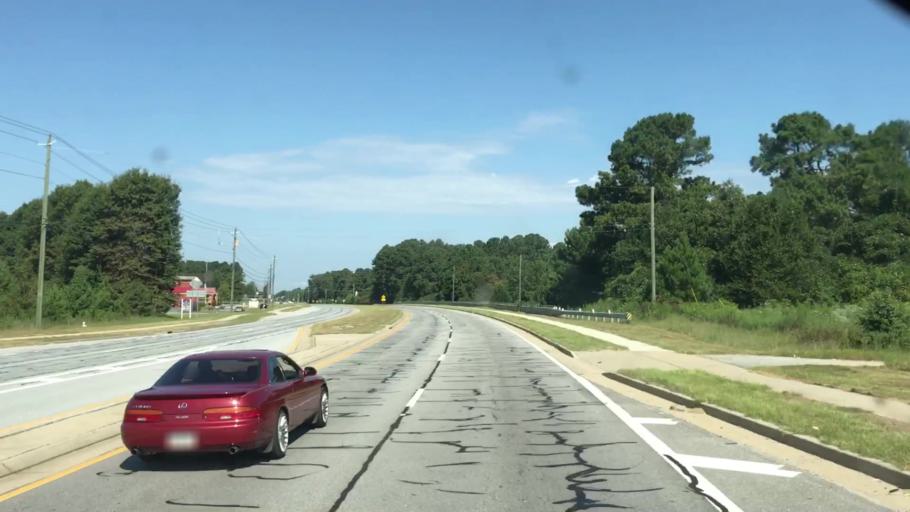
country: US
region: Georgia
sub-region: Walton County
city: Loganville
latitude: 33.8677
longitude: -83.9114
